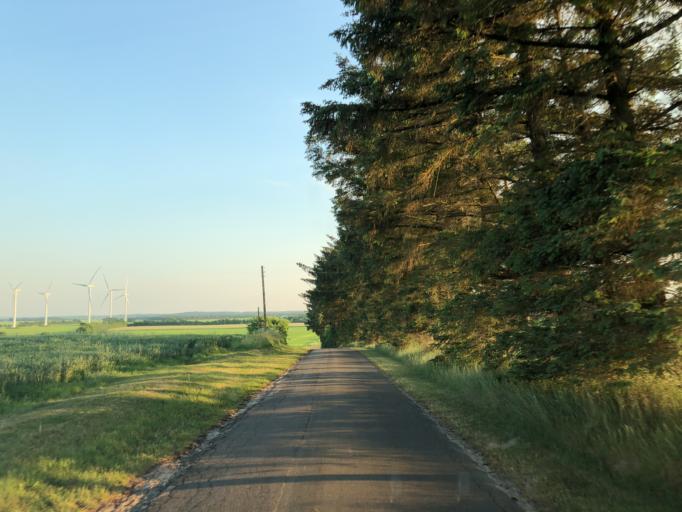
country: DK
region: Central Jutland
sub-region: Holstebro Kommune
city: Holstebro
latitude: 56.3884
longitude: 8.4721
